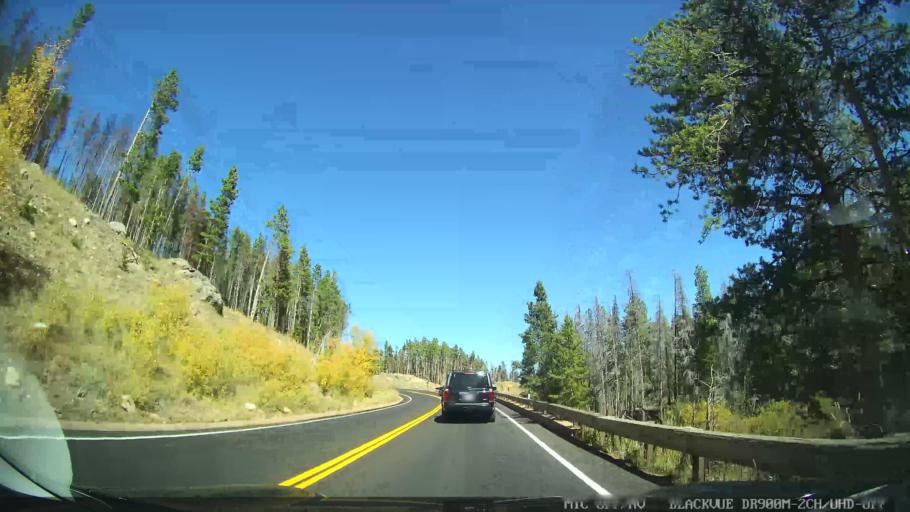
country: US
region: Colorado
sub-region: Larimer County
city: Estes Park
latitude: 40.3327
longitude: -105.5991
